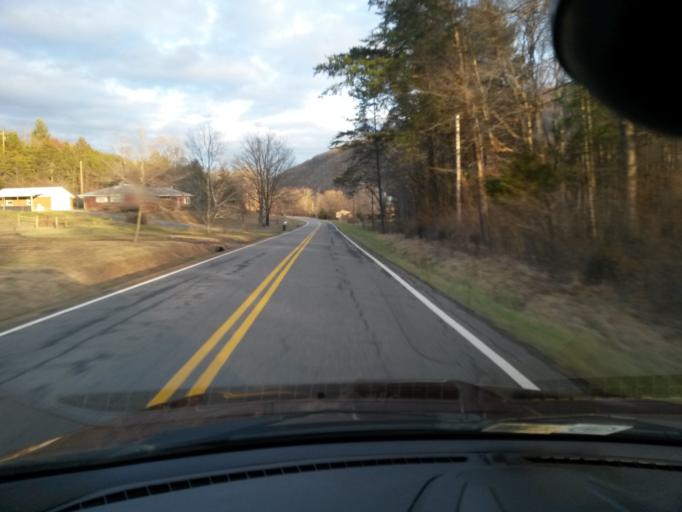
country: US
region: Virginia
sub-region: City of Covington
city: Covington
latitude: 37.7916
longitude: -80.0935
